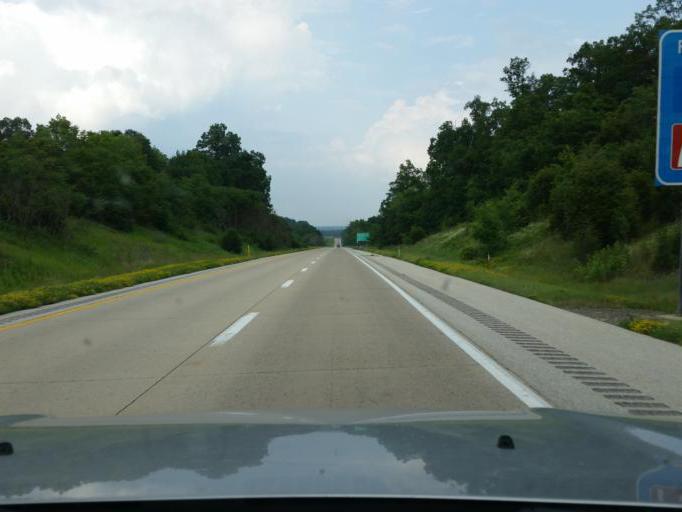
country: US
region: Pennsylvania
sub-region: Adams County
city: Gettysburg
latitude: 39.7677
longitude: -77.2508
